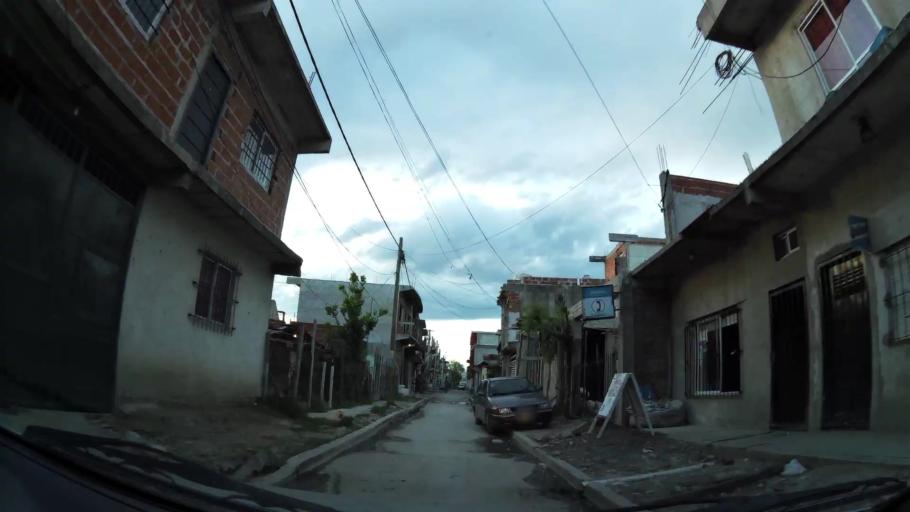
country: AR
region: Buenos Aires
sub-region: Partido de Avellaneda
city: Avellaneda
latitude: -34.6806
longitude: -58.3268
